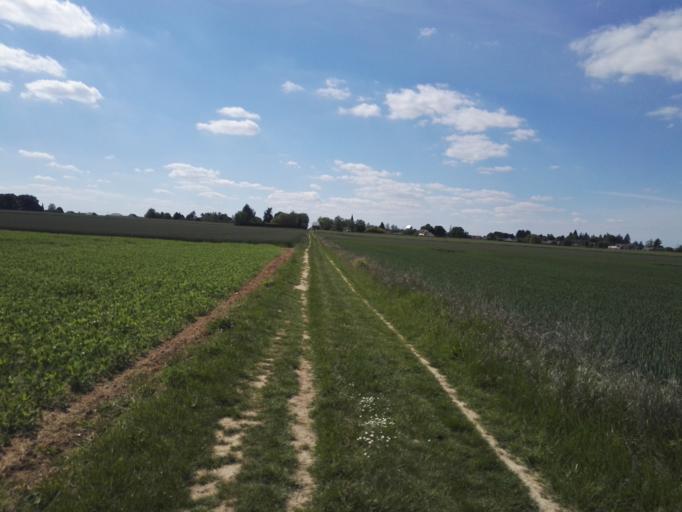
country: FR
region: Haute-Normandie
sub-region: Departement de l'Eure
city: Menilles
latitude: 49.0054
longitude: 1.3160
